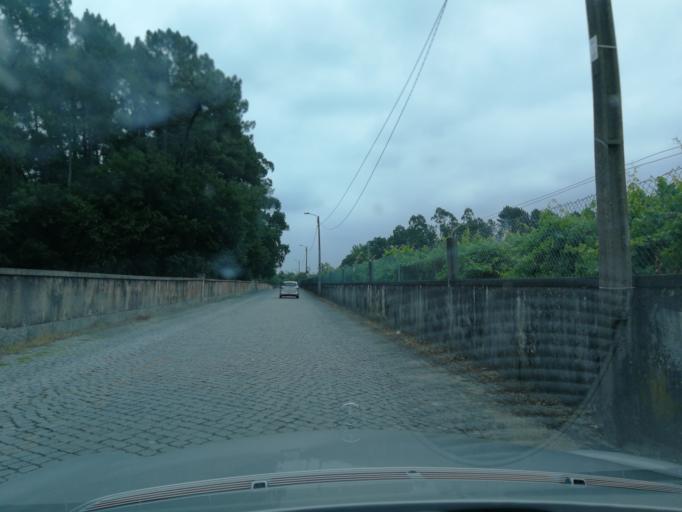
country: PT
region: Braga
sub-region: Vila Verde
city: Prado
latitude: 41.6009
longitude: -8.4434
